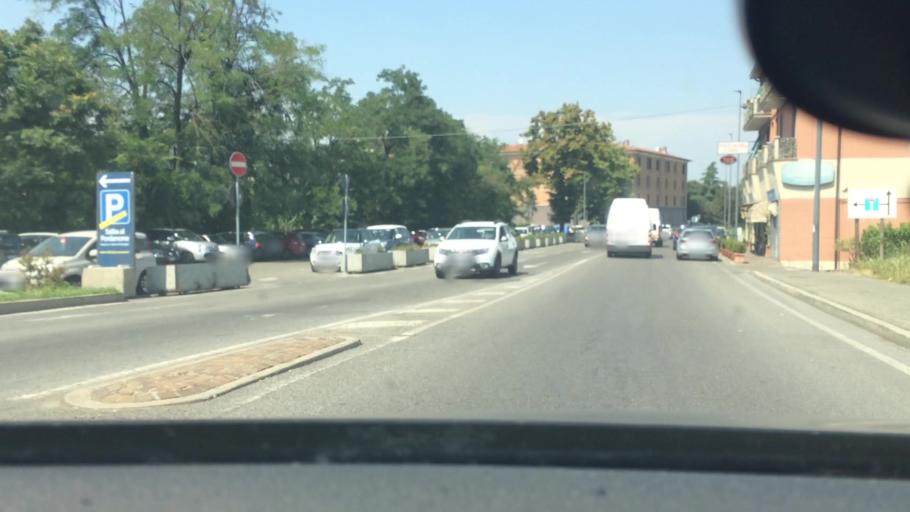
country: IT
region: Emilia-Romagna
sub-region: Provincia di Piacenza
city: Piacenza
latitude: 45.0570
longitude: 9.6783
